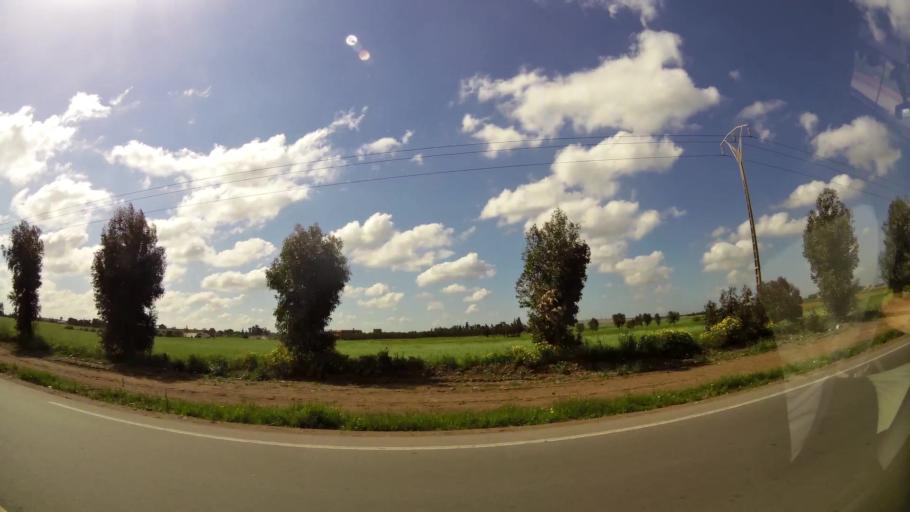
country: MA
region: Grand Casablanca
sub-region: Mediouna
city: Mediouna
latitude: 33.4170
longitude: -7.5296
